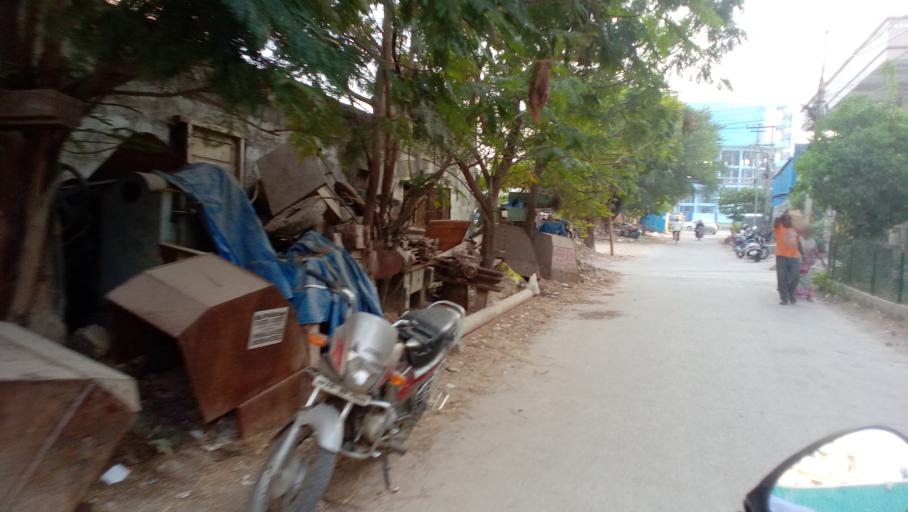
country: IN
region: Telangana
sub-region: Medak
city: Serilingampalle
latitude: 17.5078
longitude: 78.3046
